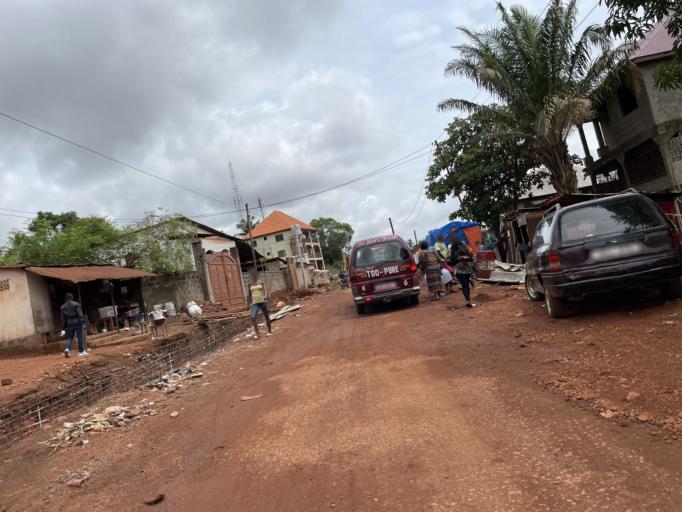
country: SL
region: Western Area
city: Hastings
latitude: 8.4149
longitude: -13.1536
